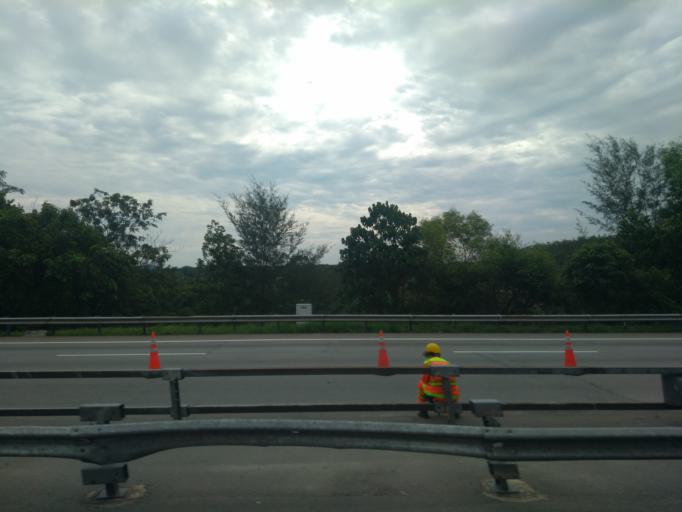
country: MY
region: Melaka
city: Alor Gajah
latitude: 2.4142
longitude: 102.2172
